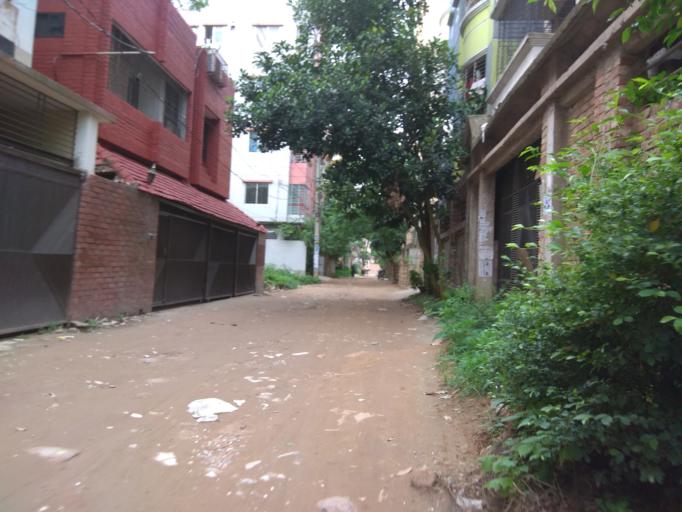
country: BD
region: Dhaka
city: Tungi
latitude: 23.8258
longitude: 90.3514
